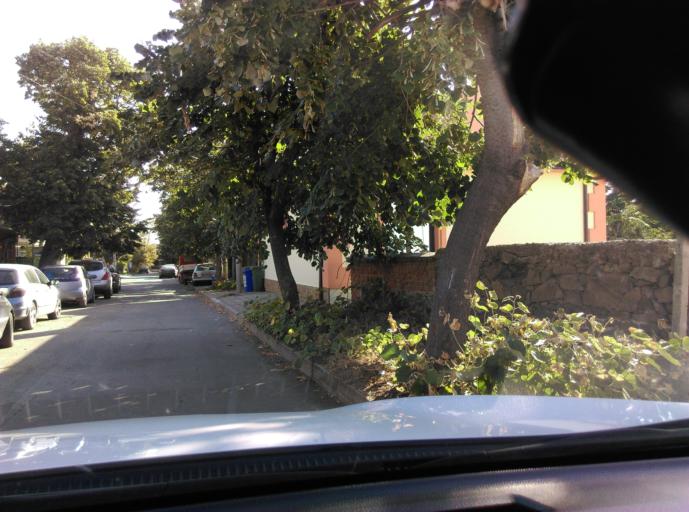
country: BG
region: Burgas
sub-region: Obshtina Kameno
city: Kameno
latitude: 42.6013
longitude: 27.3851
